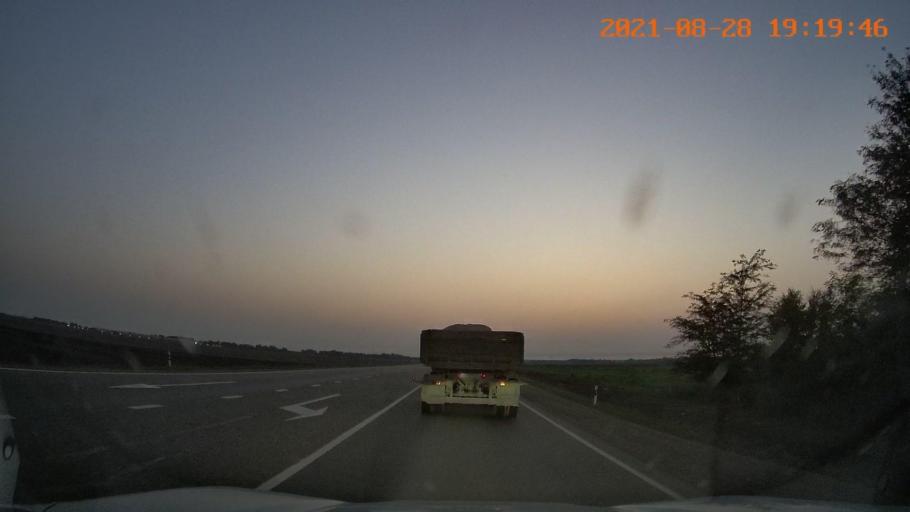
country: RU
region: Krasnodarskiy
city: Ryazanskaya
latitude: 44.8905
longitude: 39.5118
